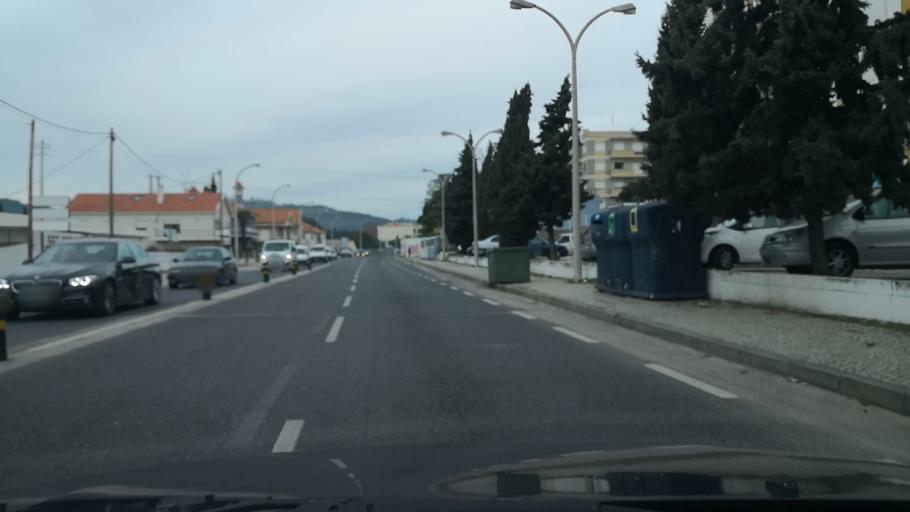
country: PT
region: Setubal
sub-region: Setubal
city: Setubal
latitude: 38.5367
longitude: -8.8847
